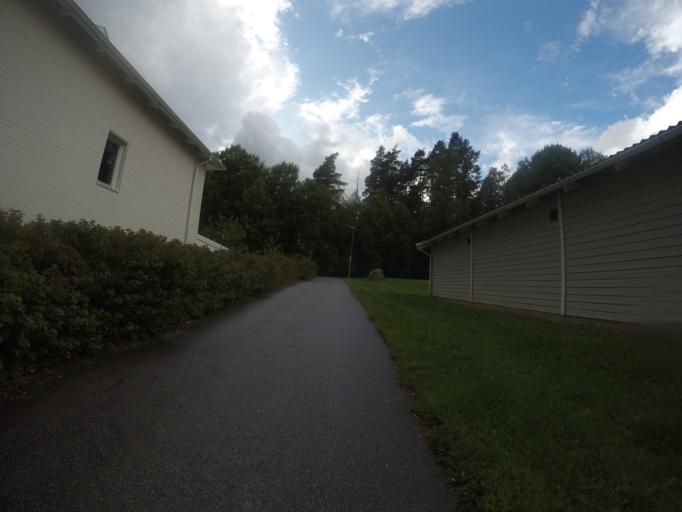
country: SE
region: Vaestmanland
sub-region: Vasteras
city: Vasteras
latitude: 59.6527
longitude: 16.5318
